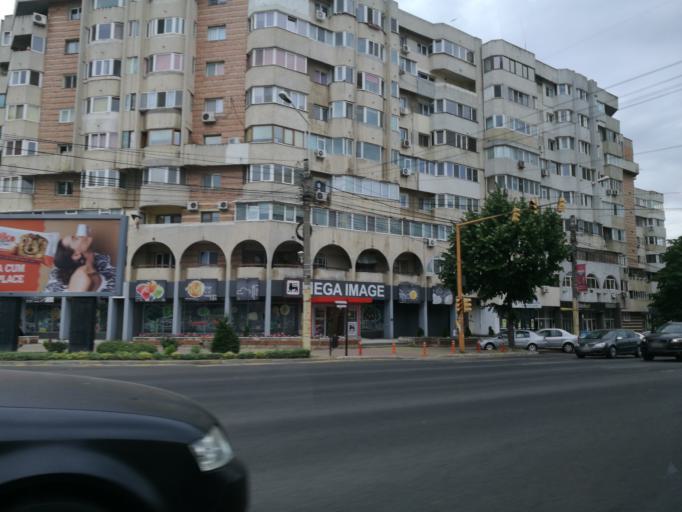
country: RO
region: Constanta
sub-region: Municipiul Constanta
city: Constanta
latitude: 44.1887
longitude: 28.6340
